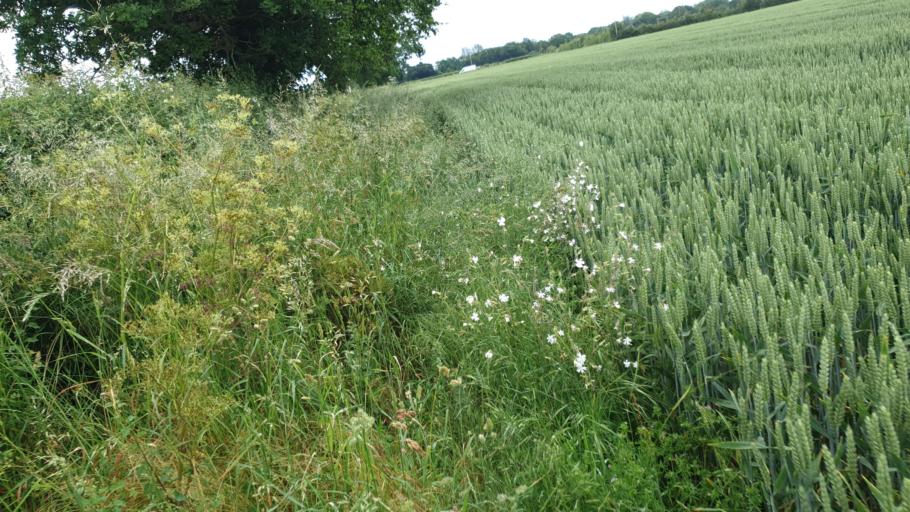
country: GB
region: England
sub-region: Essex
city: Great Bentley
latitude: 51.8803
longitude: 1.1125
